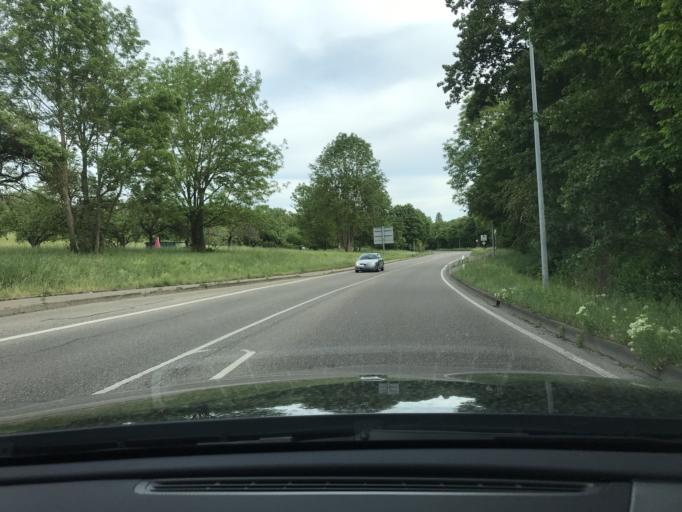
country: DE
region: Baden-Wuerttemberg
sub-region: Regierungsbezirk Stuttgart
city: Waiblingen
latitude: 48.8277
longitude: 9.3302
